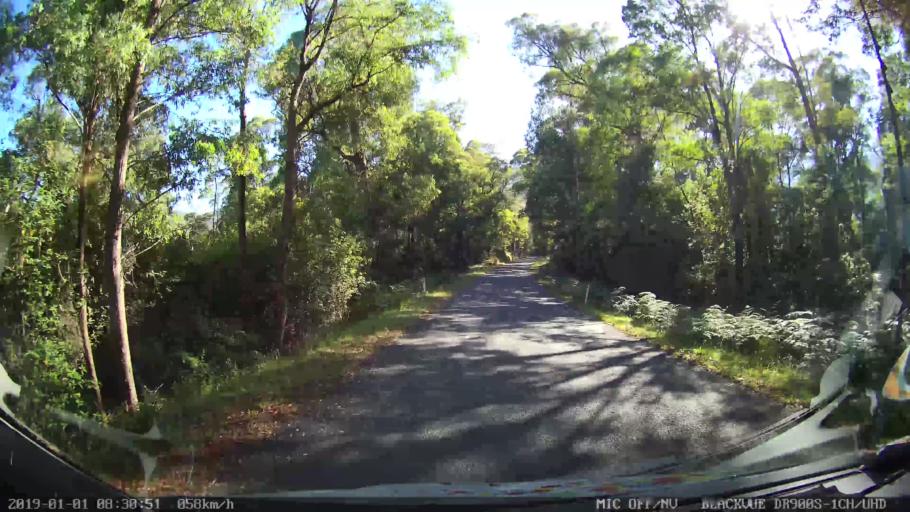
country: AU
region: New South Wales
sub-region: Snowy River
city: Jindabyne
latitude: -36.3733
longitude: 148.2007
